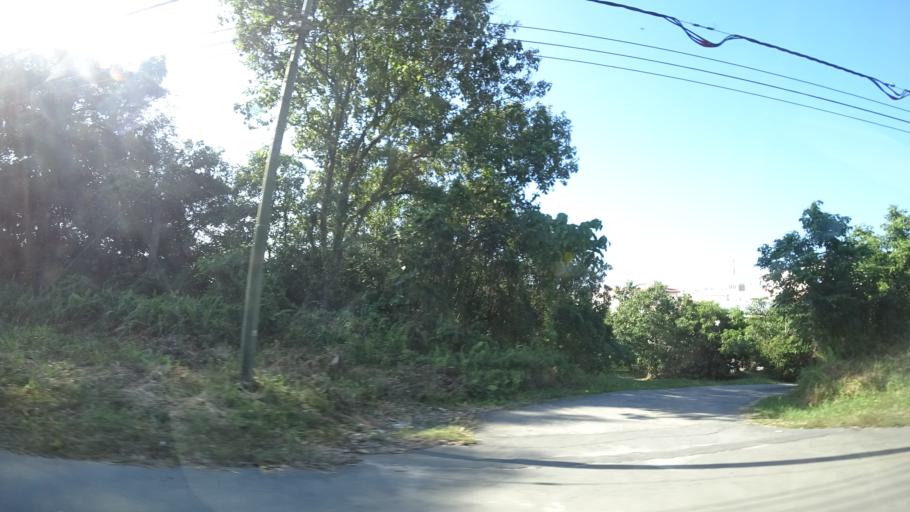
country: BN
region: Belait
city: Seria
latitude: 4.6796
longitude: 114.4985
